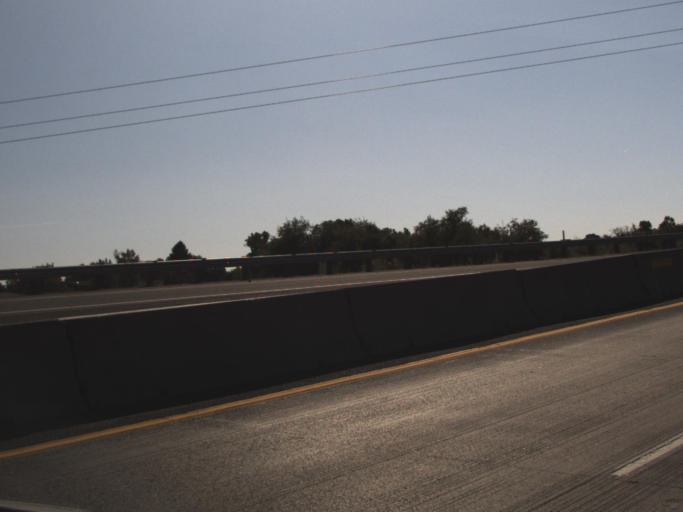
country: US
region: Washington
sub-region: Benton County
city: Kennewick
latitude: 46.2156
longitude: -119.1399
